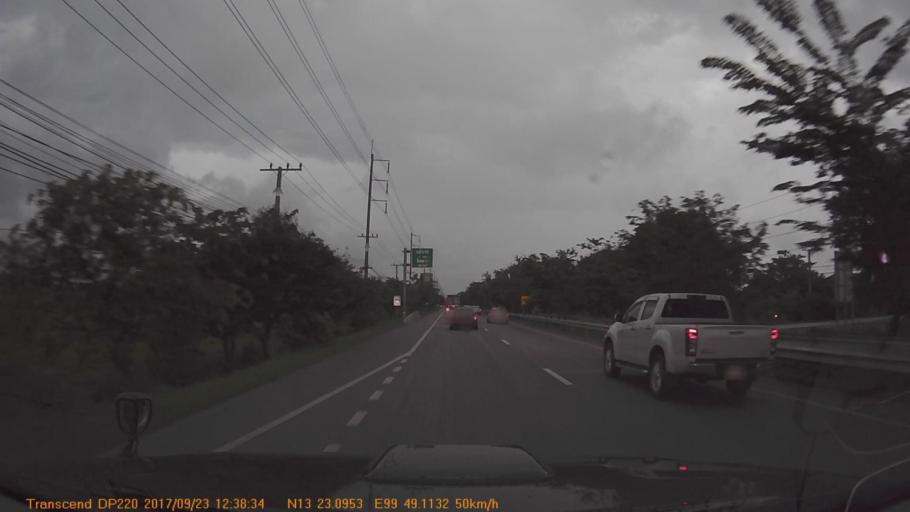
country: TH
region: Ratchaburi
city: Pak Tho
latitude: 13.3848
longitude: 99.8186
